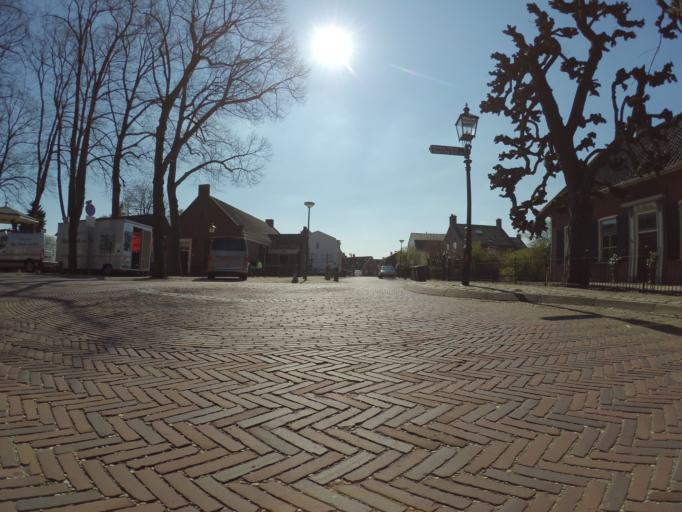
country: NL
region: Utrecht
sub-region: Gemeente Utrechtse Heuvelrug
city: Driebergen-Rijsenburg
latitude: 52.0240
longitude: 5.2449
